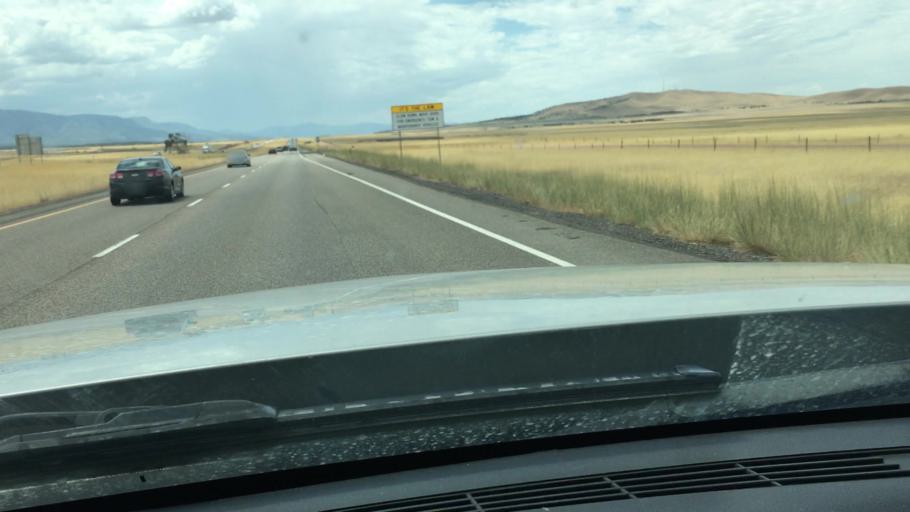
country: US
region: Utah
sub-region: Millard County
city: Fillmore
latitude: 39.0756
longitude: -112.2805
